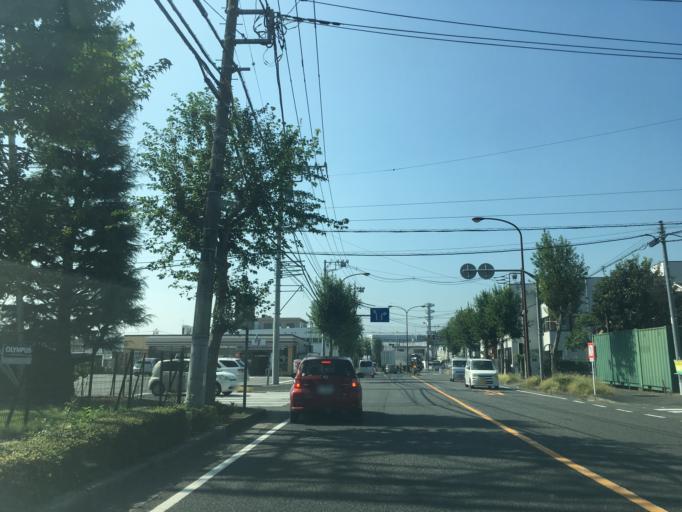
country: JP
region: Tokyo
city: Hachioji
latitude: 35.6671
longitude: 139.3583
